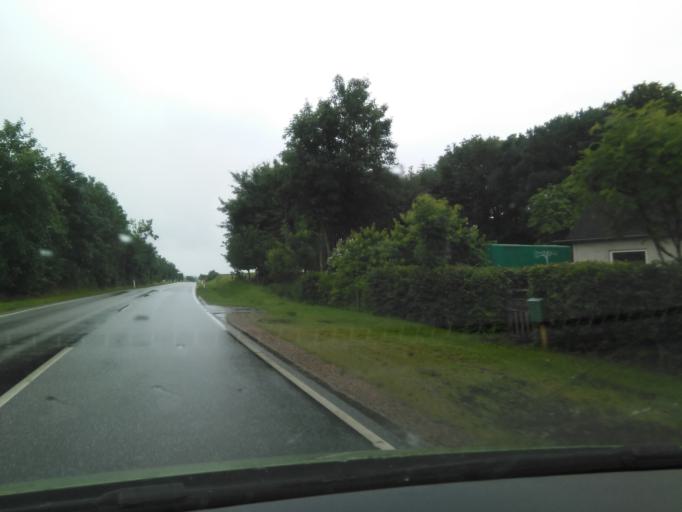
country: DK
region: Central Jutland
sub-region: Skanderborg Kommune
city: Ry
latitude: 55.9901
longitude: 9.7668
